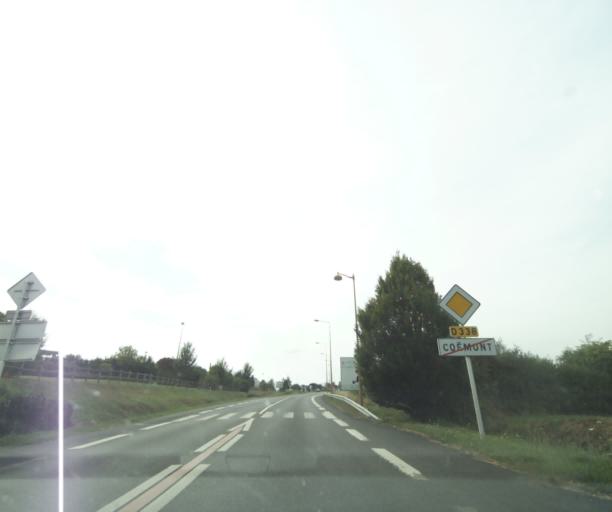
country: FR
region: Pays de la Loire
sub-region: Departement de la Sarthe
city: Chateau-du-Loir
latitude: 47.6875
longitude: 0.4350
